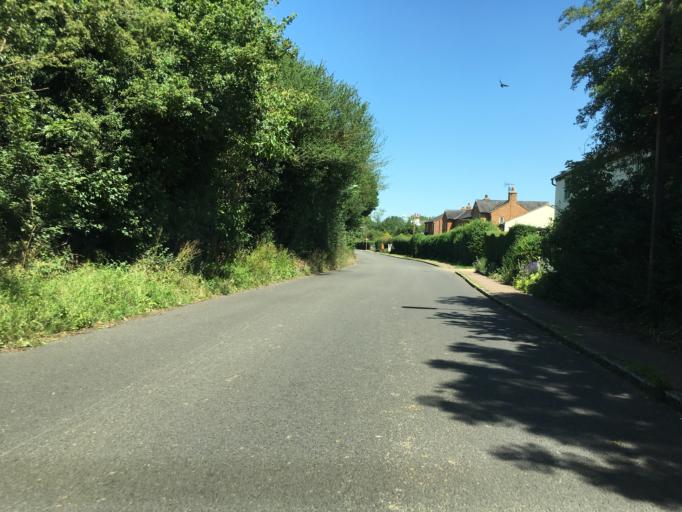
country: GB
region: England
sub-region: Milton Keynes
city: Simpson
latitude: 52.0328
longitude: -0.7241
